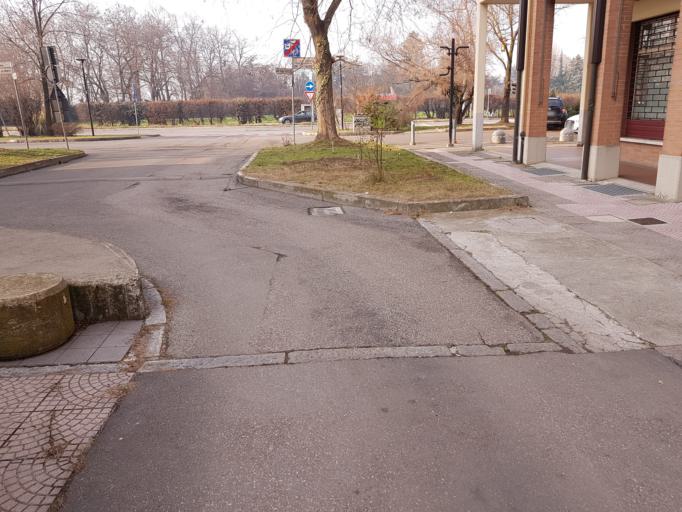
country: IT
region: Emilia-Romagna
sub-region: Provincia di Bologna
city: Quarto Inferiore
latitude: 44.5115
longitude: 11.3855
